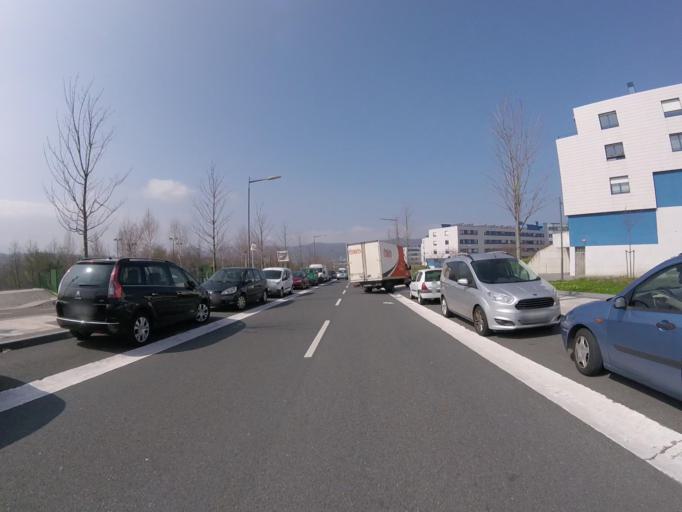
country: ES
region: Basque Country
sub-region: Provincia de Guipuzcoa
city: San Sebastian
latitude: 43.2986
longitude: -1.9926
